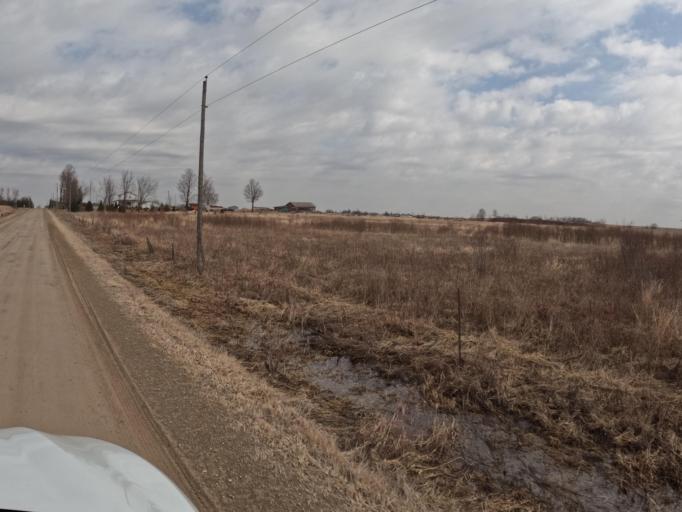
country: CA
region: Ontario
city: Orangeville
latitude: 43.9377
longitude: -80.2218
